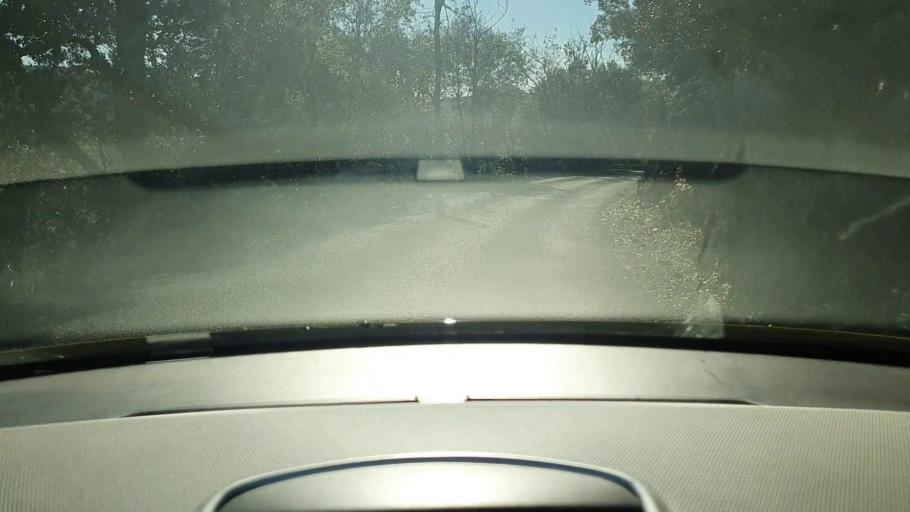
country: FR
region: Languedoc-Roussillon
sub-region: Departement du Gard
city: Sumene
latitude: 44.0257
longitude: 3.6941
